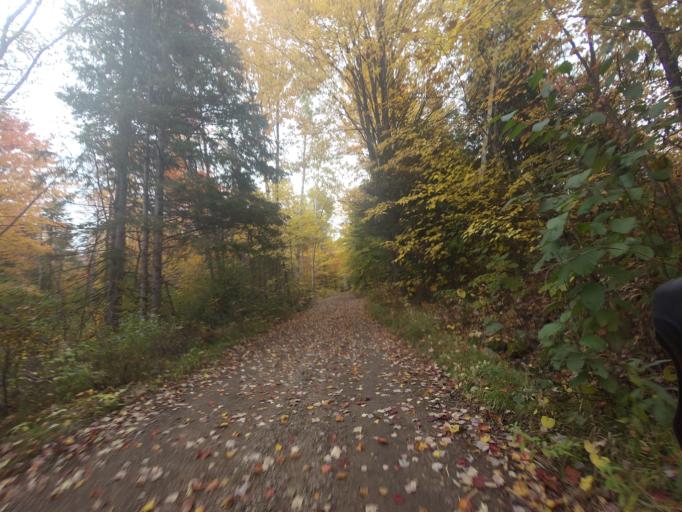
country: CA
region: Ontario
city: Pembroke
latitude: 45.7276
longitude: -77.2267
